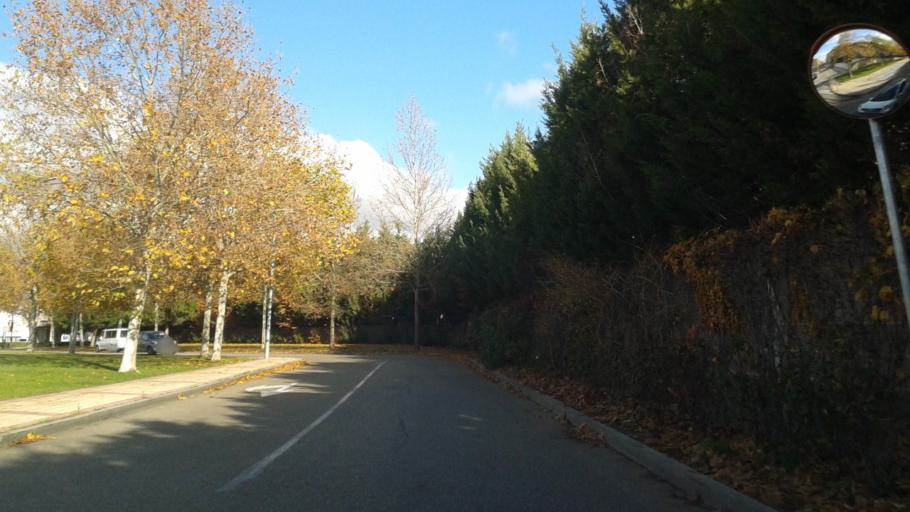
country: ES
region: Castille and Leon
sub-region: Provincia de Valladolid
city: Arroyo
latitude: 41.6206
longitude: -4.7741
